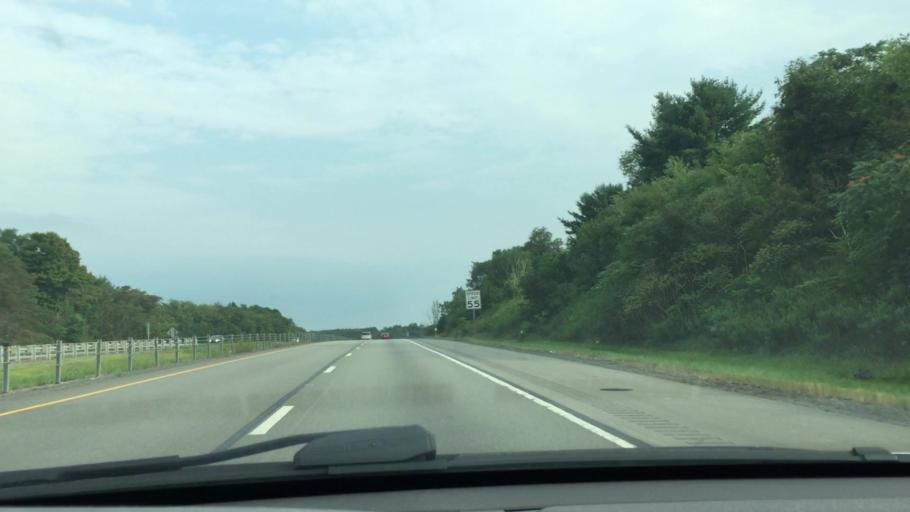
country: US
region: Pennsylvania
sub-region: Beaver County
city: Beaver
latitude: 40.6963
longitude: -80.3606
